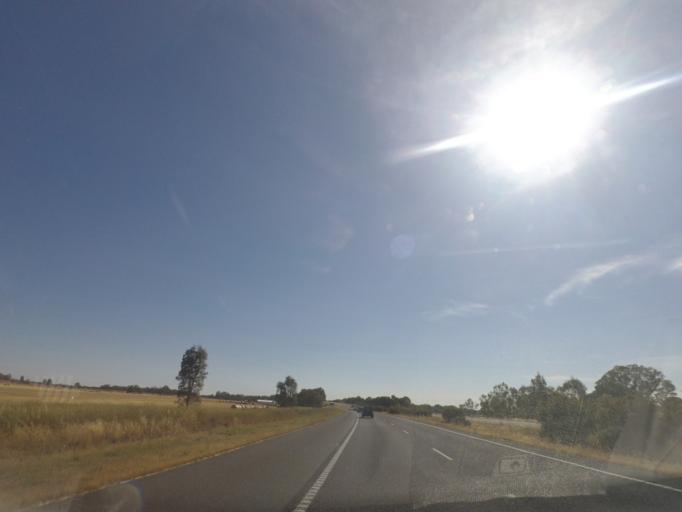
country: AU
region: Victoria
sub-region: Greater Shepparton
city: Shepparton
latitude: -36.6760
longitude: 145.2469
